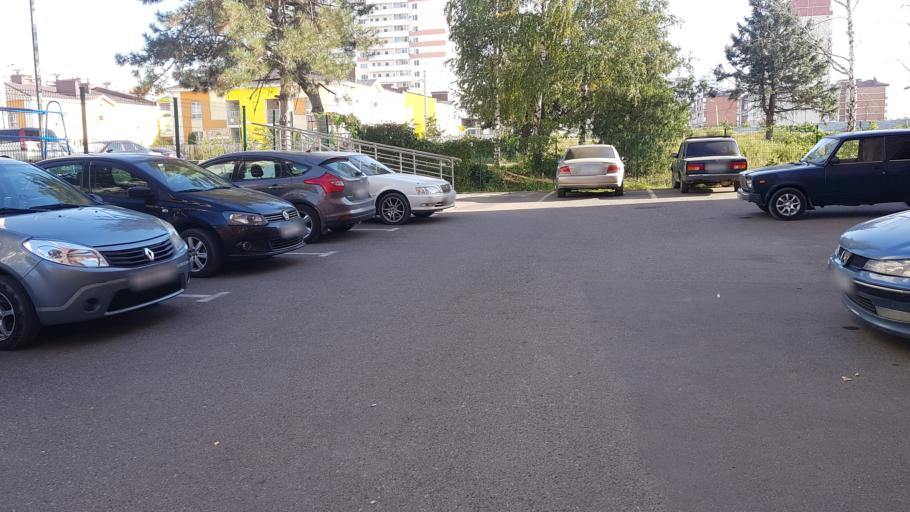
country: RU
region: Krasnodarskiy
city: Novotitarovskaya
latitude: 45.1444
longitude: 38.9930
